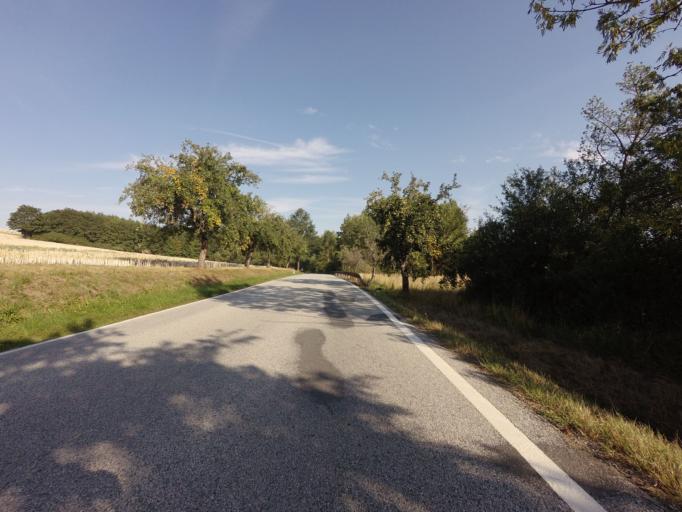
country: CZ
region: Jihocesky
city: Tyn nad Vltavou
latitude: 49.2615
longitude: 14.4130
